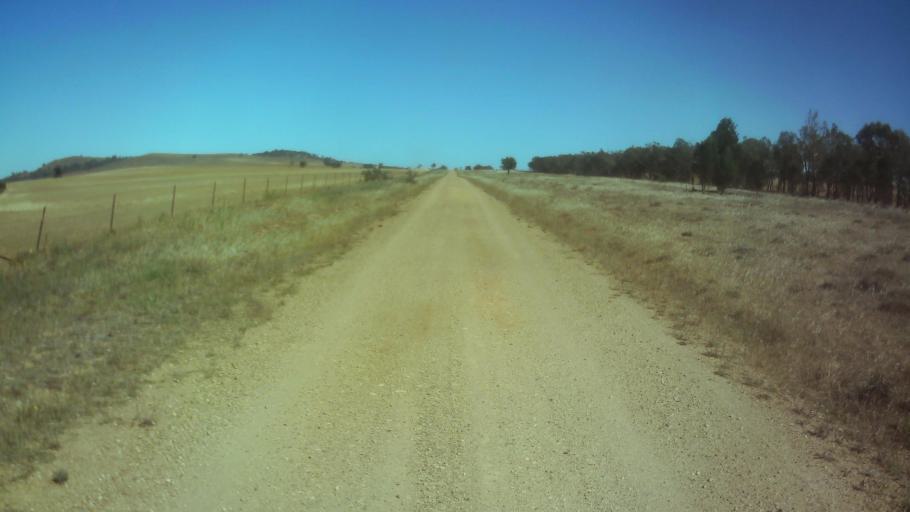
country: AU
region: New South Wales
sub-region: Weddin
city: Grenfell
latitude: -33.9694
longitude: 148.3159
